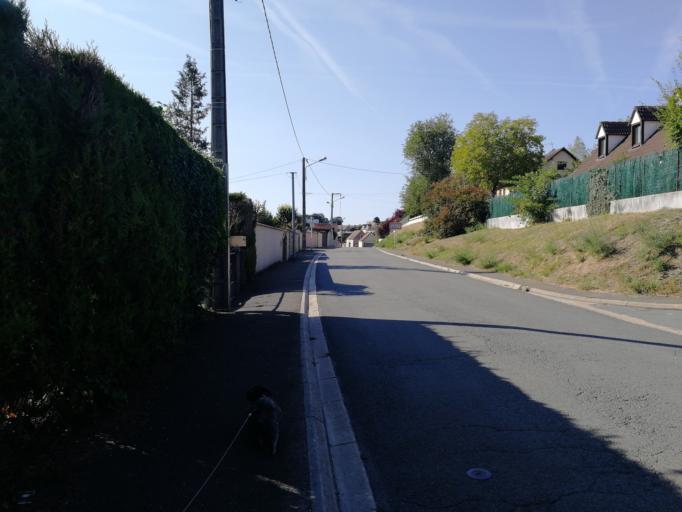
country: FR
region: Centre
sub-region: Departement d'Eure-et-Loir
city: Gallardon
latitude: 48.5270
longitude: 1.6789
